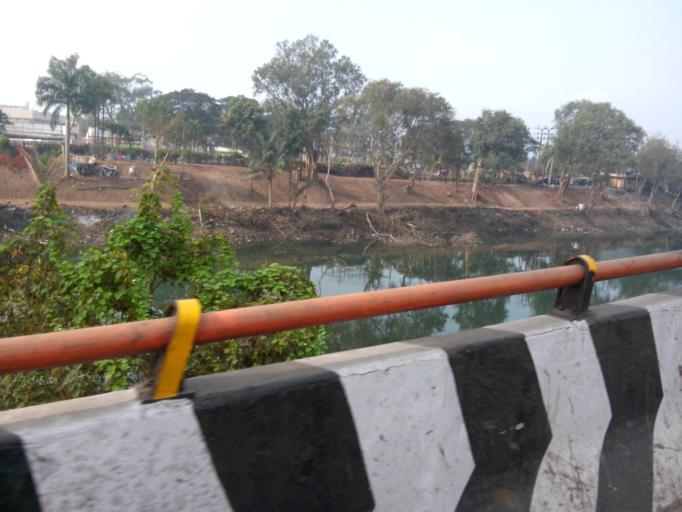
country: IN
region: Andhra Pradesh
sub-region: Krishna
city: Vijayawada
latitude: 16.5111
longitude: 80.6167
